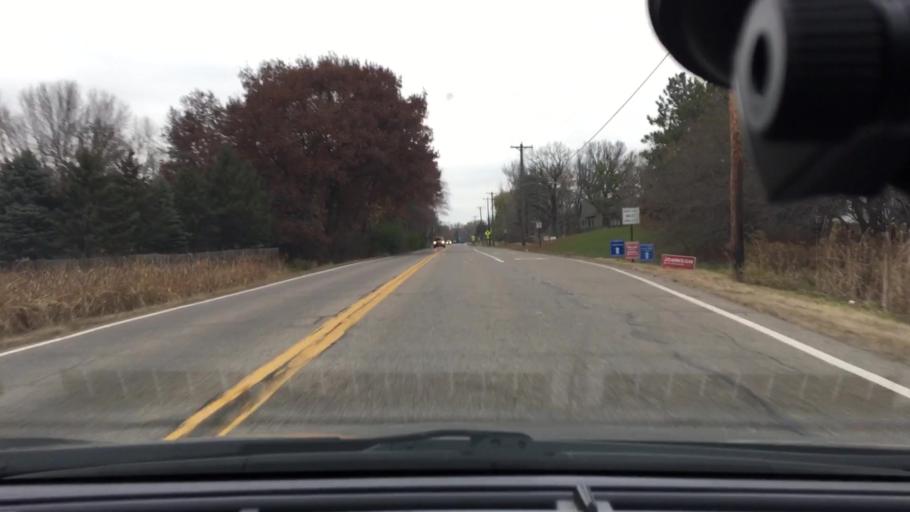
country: US
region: Minnesota
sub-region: Hennepin County
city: Corcoran
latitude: 45.1023
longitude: -93.5121
